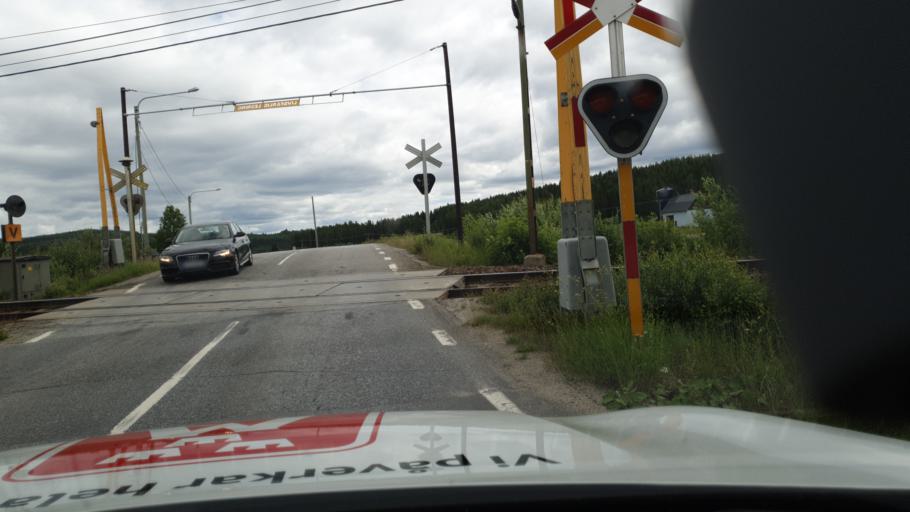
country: SE
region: Vaesterbotten
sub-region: Vannas Kommun
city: Vaennaes
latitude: 63.8975
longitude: 19.6984
